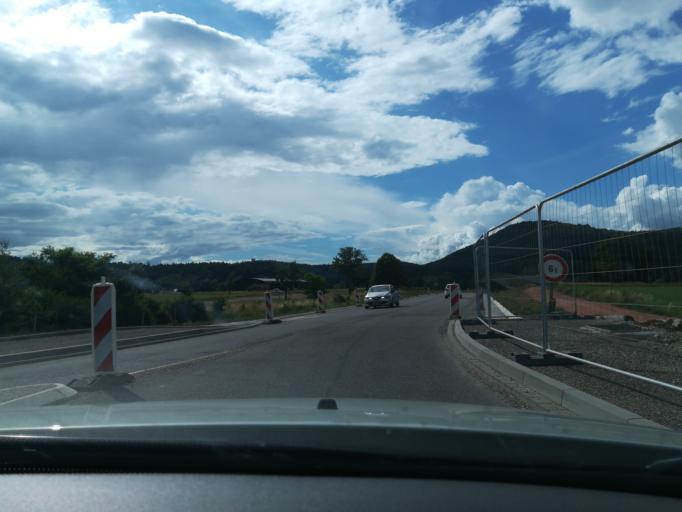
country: FR
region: Alsace
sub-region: Departement du Bas-Rhin
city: Dossenheim-sur-Zinsel
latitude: 48.7997
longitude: 7.4051
